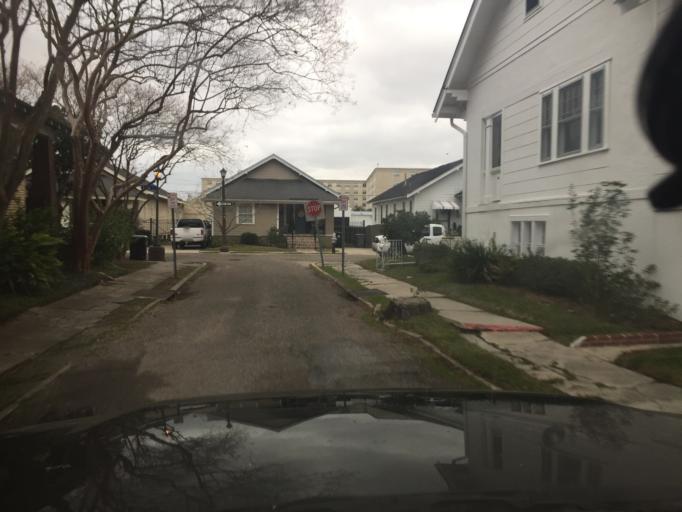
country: US
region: Louisiana
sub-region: Orleans Parish
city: New Orleans
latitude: 29.9830
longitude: -90.0860
